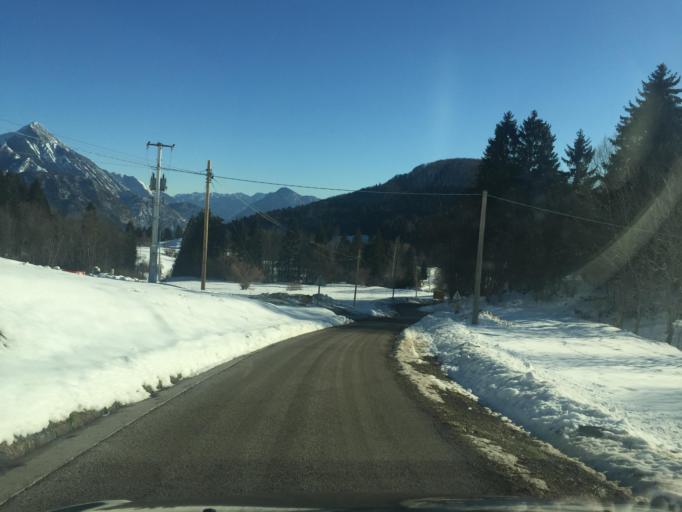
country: IT
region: Friuli Venezia Giulia
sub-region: Provincia di Udine
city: Lauco
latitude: 46.4299
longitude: 12.9749
